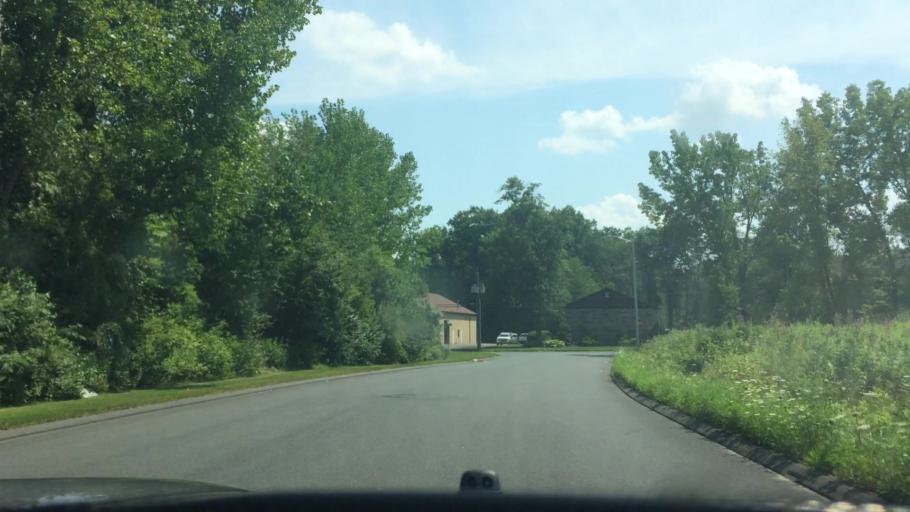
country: US
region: Connecticut
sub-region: Hartford County
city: Tariffville
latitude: 41.8581
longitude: -72.7363
